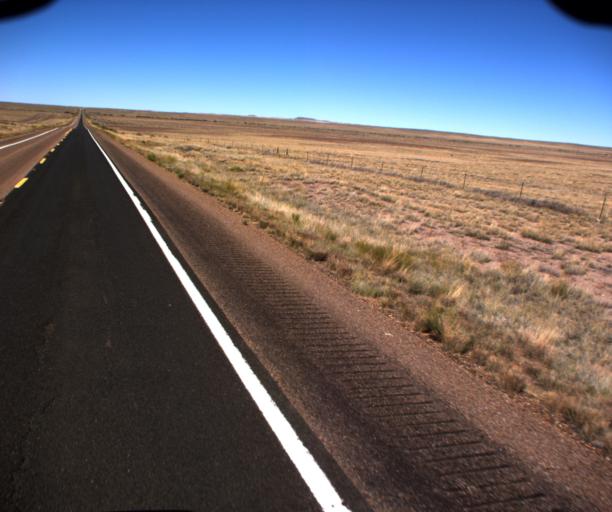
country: US
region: Arizona
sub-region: Navajo County
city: Snowflake
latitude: 34.7279
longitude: -109.7796
